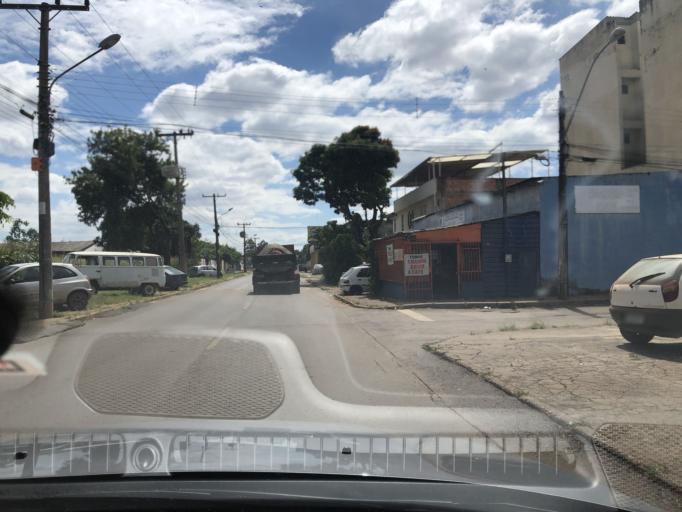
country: BR
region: Federal District
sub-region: Brasilia
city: Brasilia
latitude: -16.0036
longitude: -48.0563
